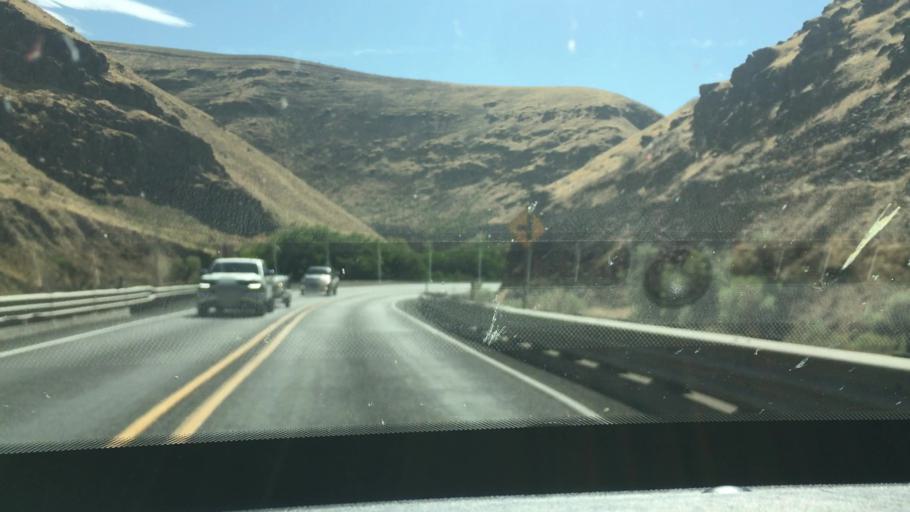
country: US
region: Washington
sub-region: Klickitat County
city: Goldendale
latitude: 45.6474
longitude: -120.8053
